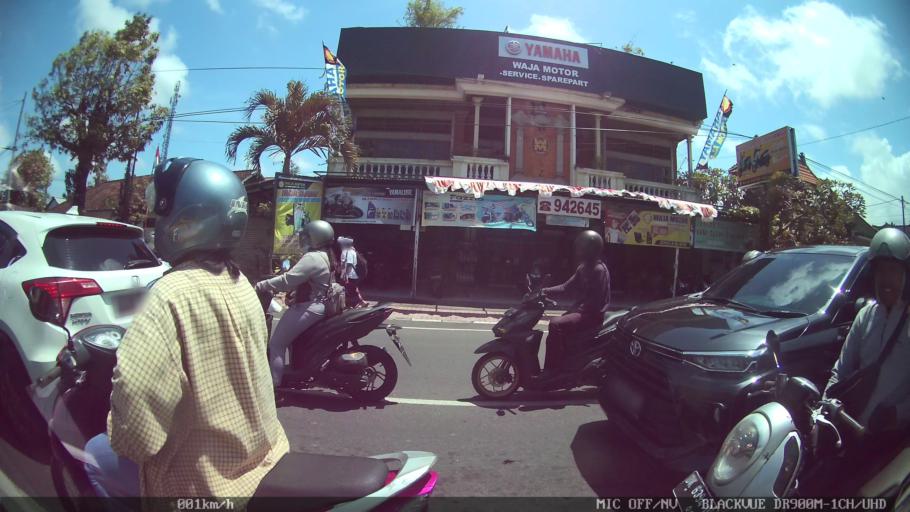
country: ID
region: Bali
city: Banjar Sedang
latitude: -8.5660
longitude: 115.3004
